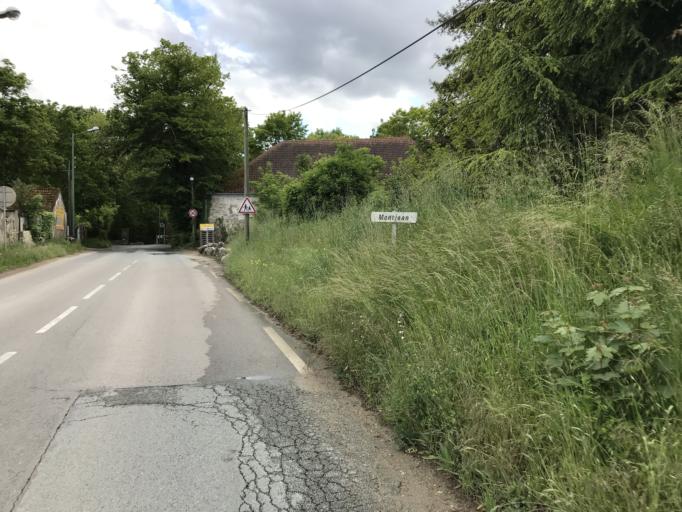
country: FR
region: Ile-de-France
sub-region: Departement du Val-de-Marne
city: Rungis
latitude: 48.7448
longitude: 2.3365
